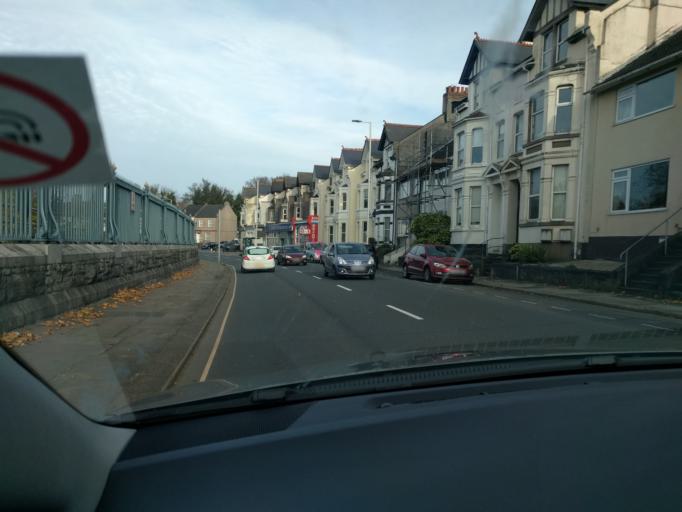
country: GB
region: England
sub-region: Cornwall
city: Torpoint
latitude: 50.3880
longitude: -4.1809
